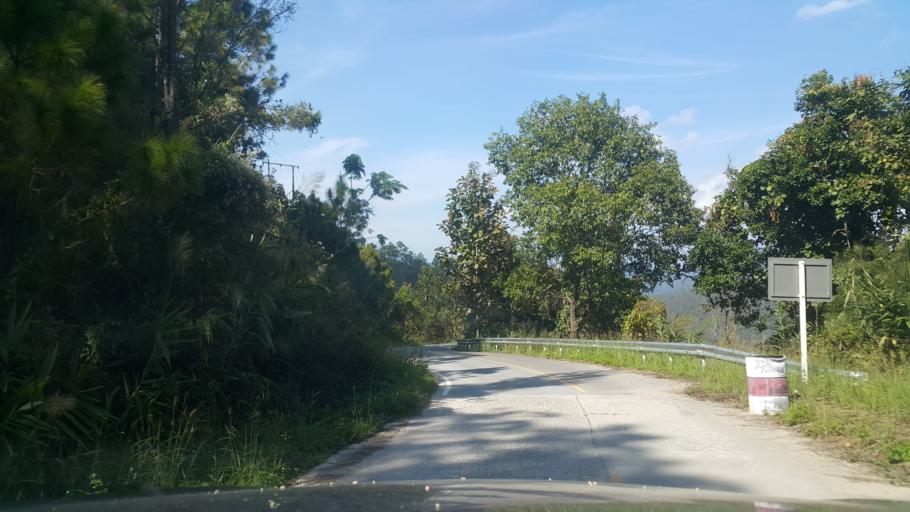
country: TH
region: Chiang Mai
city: Samoeng
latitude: 18.9127
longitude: 98.6733
